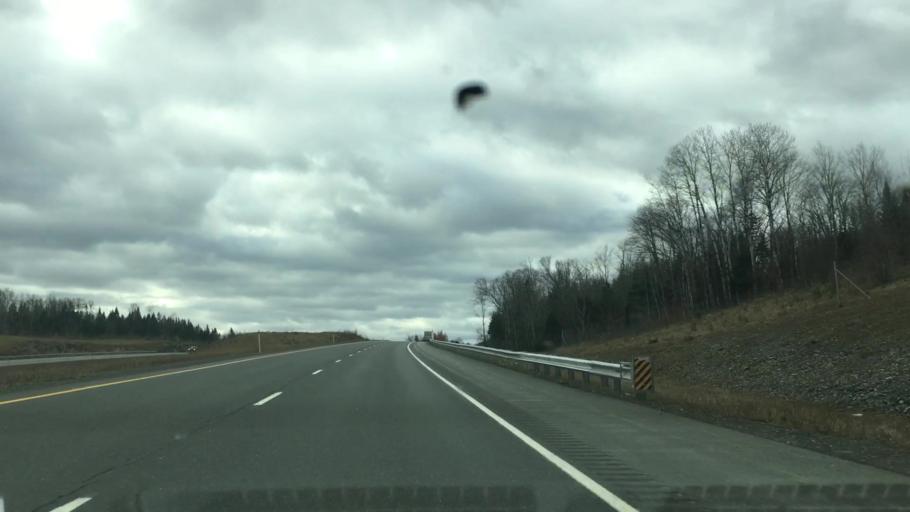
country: US
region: Maine
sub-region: Aroostook County
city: Fort Fairfield
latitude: 46.6609
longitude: -67.7325
